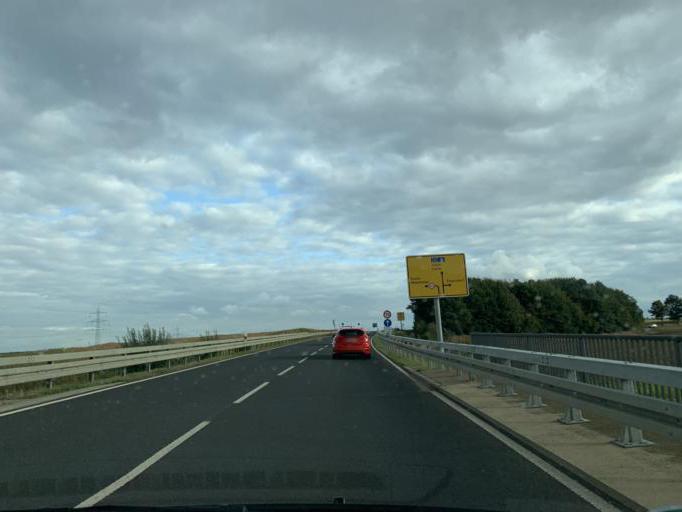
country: DE
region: North Rhine-Westphalia
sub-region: Regierungsbezirk Koln
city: Aldenhoven
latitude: 50.9233
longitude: 6.3076
